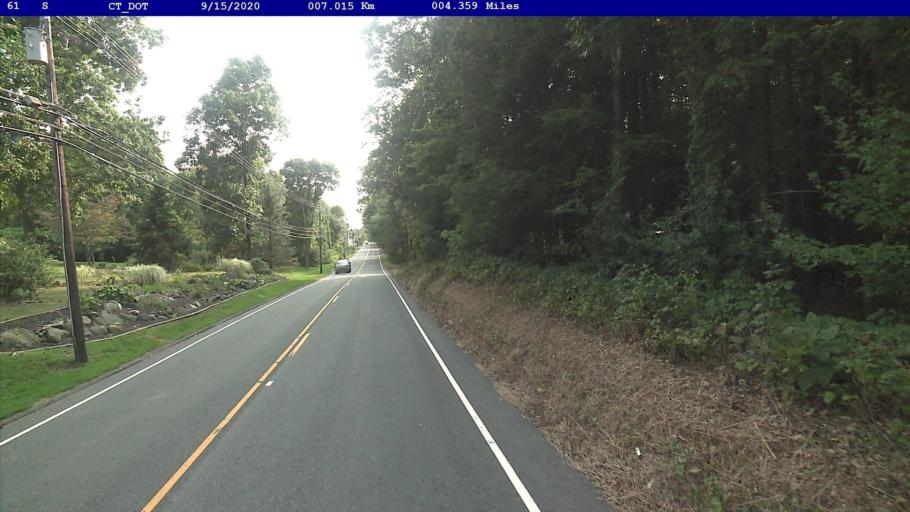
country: US
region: Connecticut
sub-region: Litchfield County
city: Bethlehem Village
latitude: 41.6431
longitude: -73.2066
